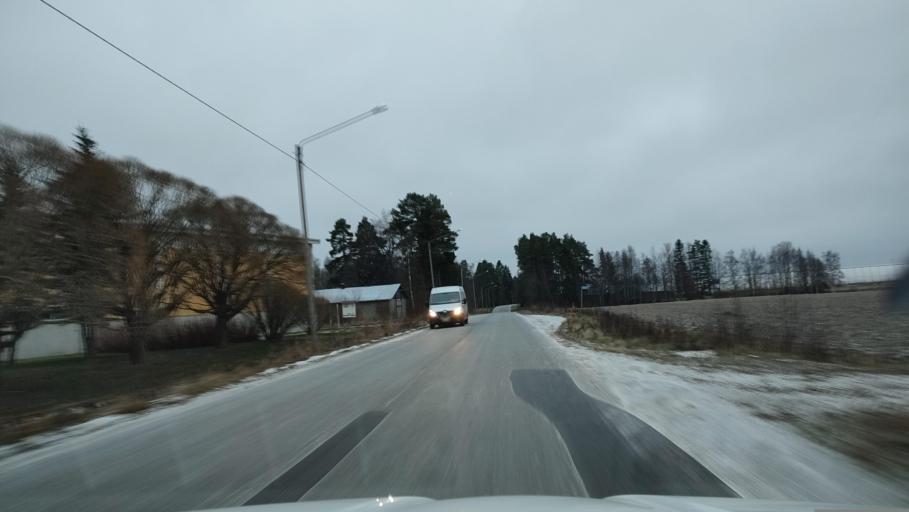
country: FI
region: Southern Ostrobothnia
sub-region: Suupohja
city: Karijoki
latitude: 62.2488
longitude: 21.6720
